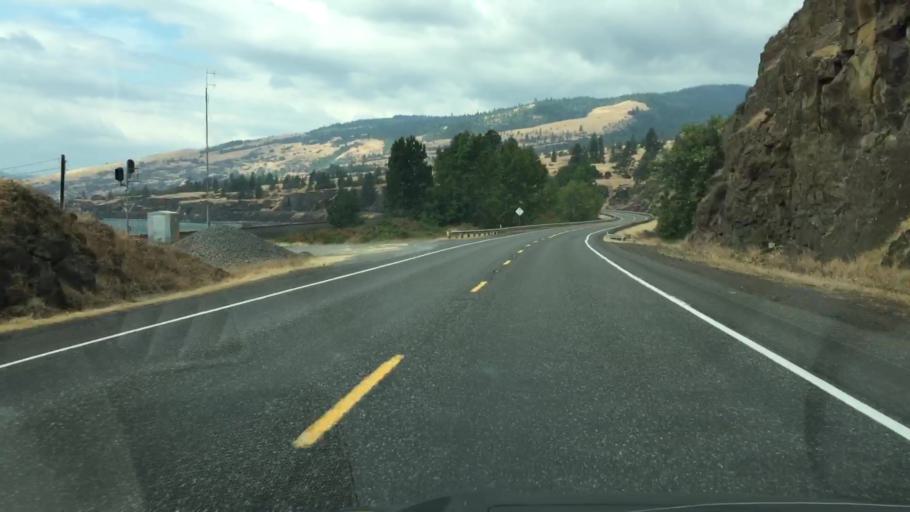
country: US
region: Oregon
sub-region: Wasco County
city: Chenoweth
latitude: 45.7093
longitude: -121.3393
